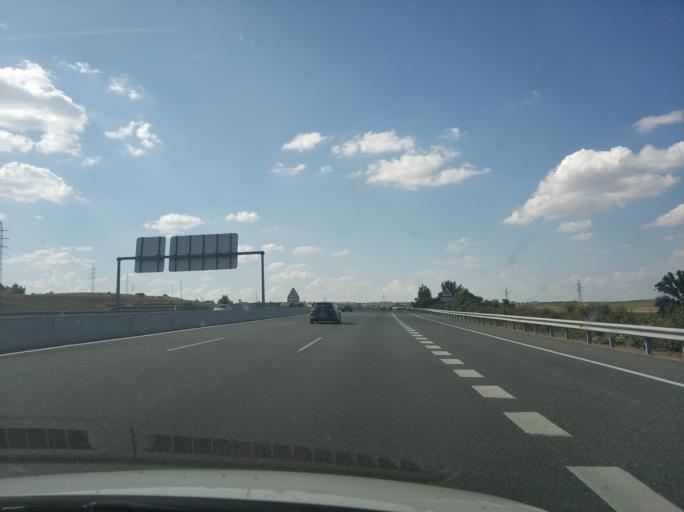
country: ES
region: Castille and Leon
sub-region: Provincia de Zamora
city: Benavente
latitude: 42.0193
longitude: -5.6680
